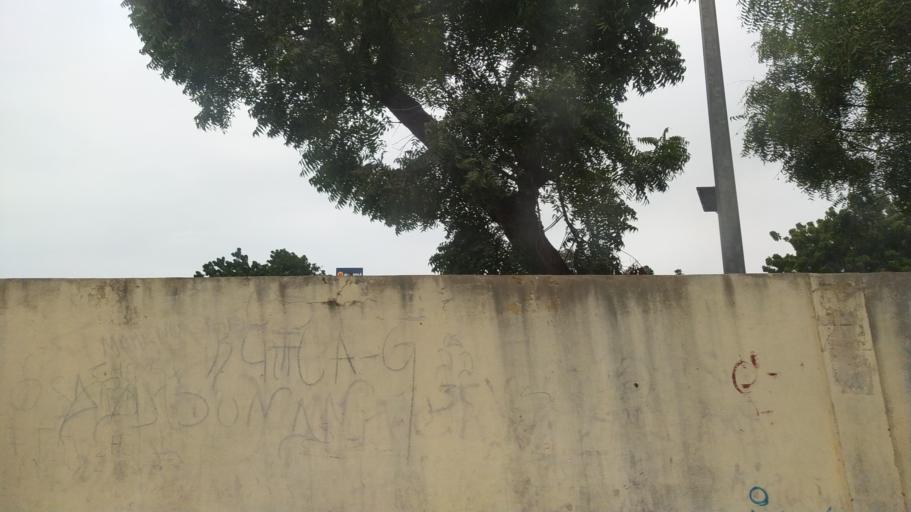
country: AO
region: Luanda
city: Luanda
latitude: -8.8879
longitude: 13.1836
